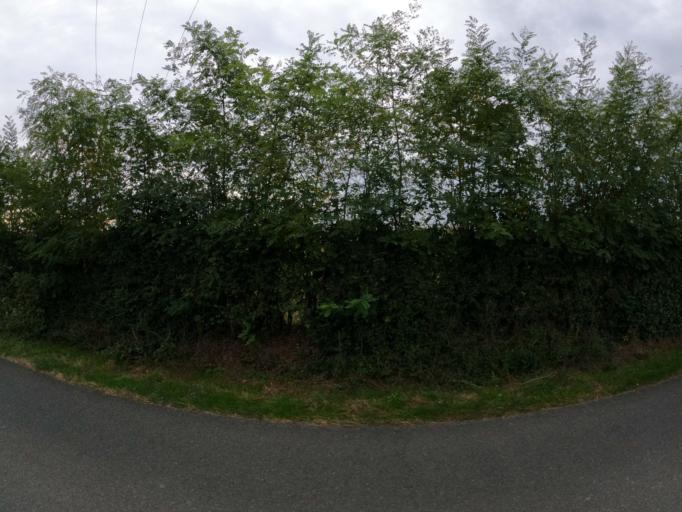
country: FR
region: Pays de la Loire
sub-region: Departement de Maine-et-Loire
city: Saint-Christophe-du-Bois
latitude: 47.0407
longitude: -0.9361
